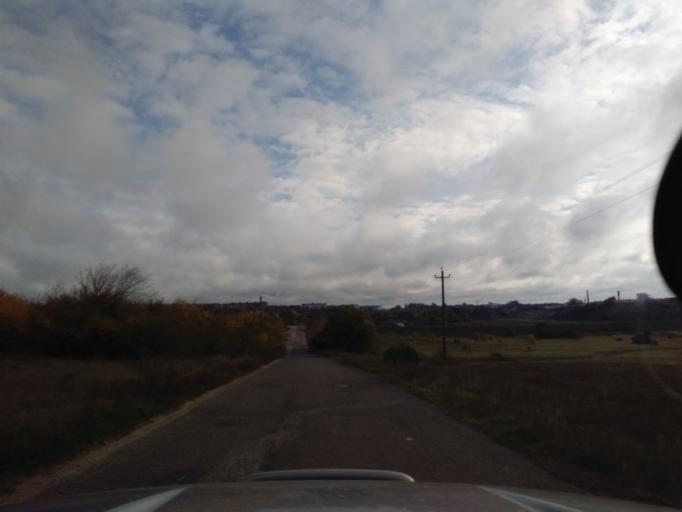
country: BY
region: Minsk
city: Kapyl'
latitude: 53.1448
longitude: 27.0725
